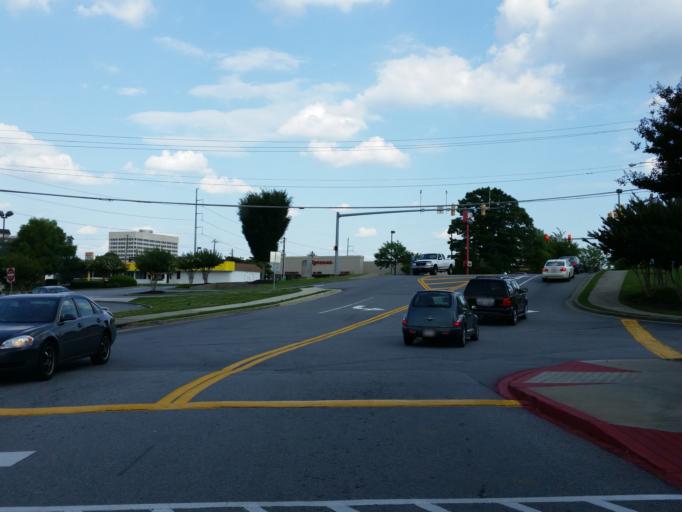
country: US
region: Georgia
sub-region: Cobb County
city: Vinings
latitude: 33.8884
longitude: -84.4762
